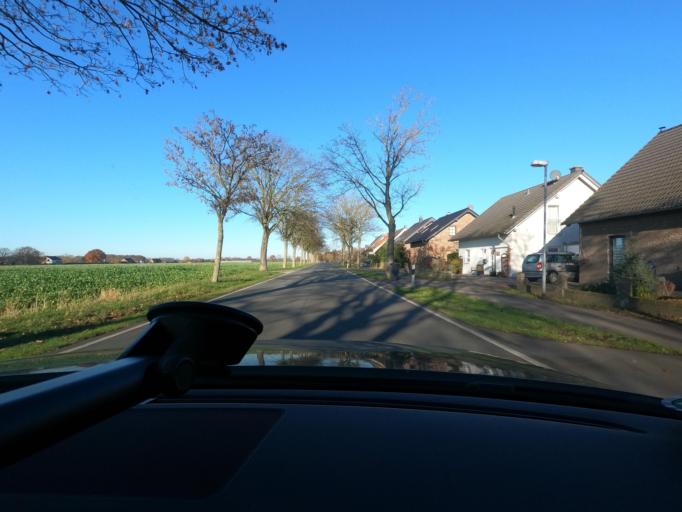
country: DE
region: North Rhine-Westphalia
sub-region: Regierungsbezirk Dusseldorf
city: Wachtendonk
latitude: 51.4629
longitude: 6.3654
